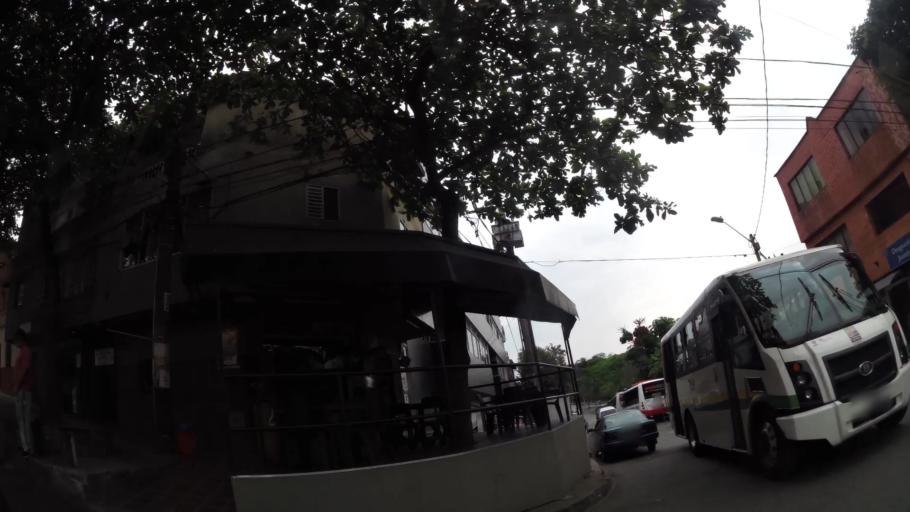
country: CO
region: Antioquia
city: Medellin
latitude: 6.2714
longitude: -75.5618
